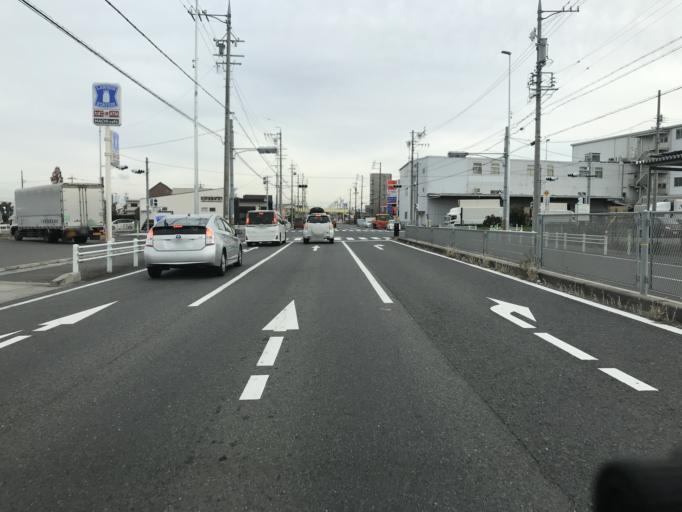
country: JP
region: Aichi
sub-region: Aisai-shi
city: Aisai
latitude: 35.1857
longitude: 136.7794
